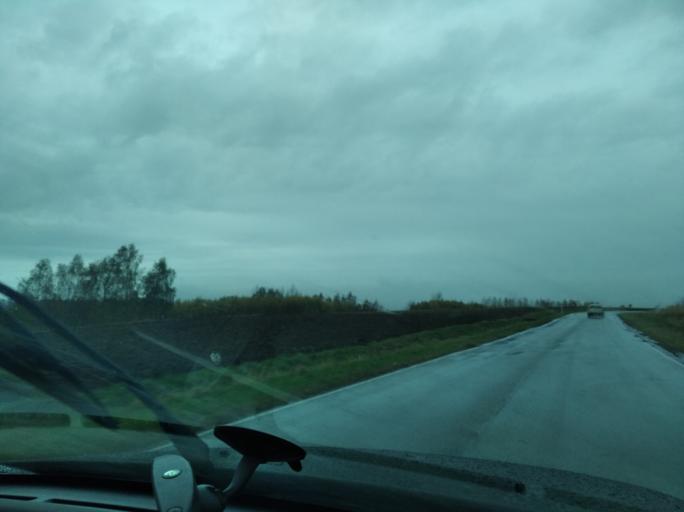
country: PL
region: Subcarpathian Voivodeship
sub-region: Powiat lancucki
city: Handzlowka
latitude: 50.0003
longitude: 22.1987
